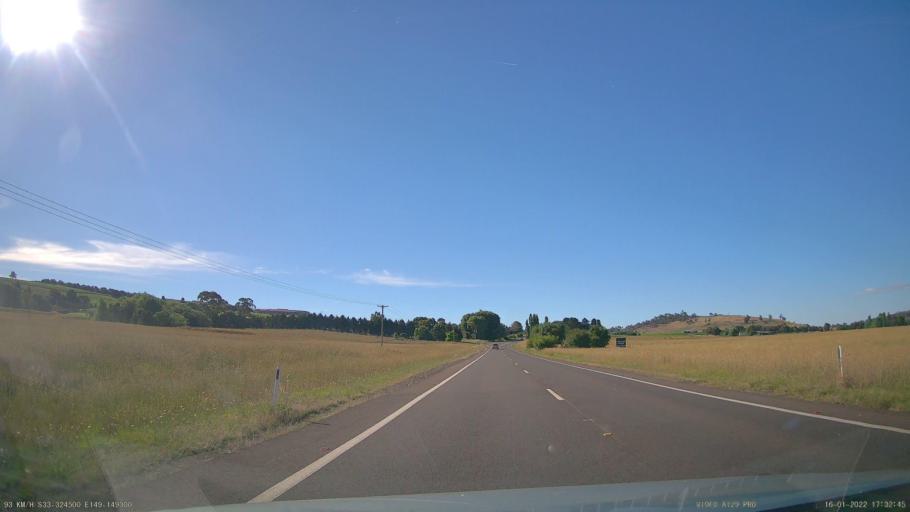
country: AU
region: New South Wales
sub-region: Orange Municipality
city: Orange
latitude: -33.3243
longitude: 149.1491
